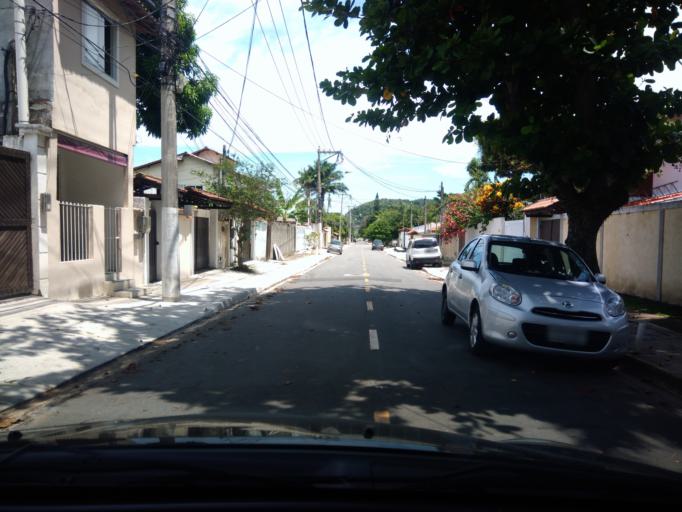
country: BR
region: Rio de Janeiro
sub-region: Niteroi
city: Niteroi
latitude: -22.9299
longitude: -43.0718
